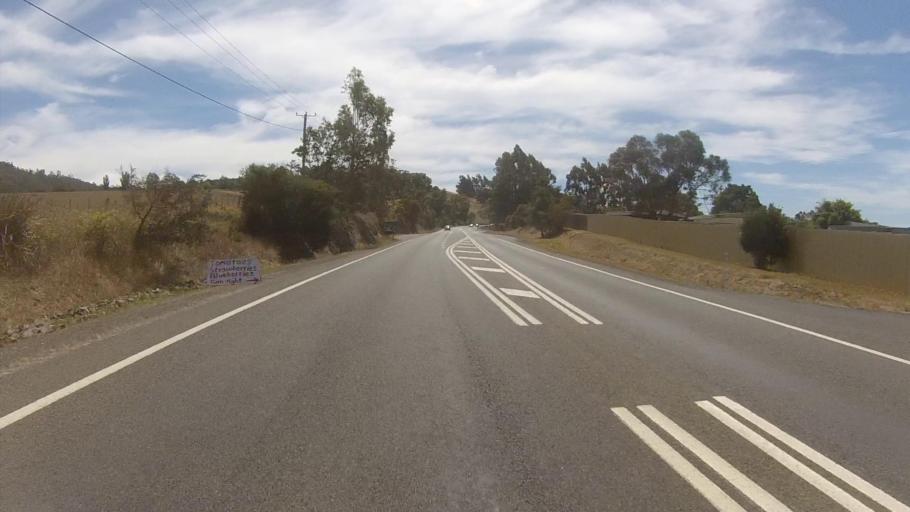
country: AU
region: Tasmania
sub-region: Kingborough
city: Margate
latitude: -43.0087
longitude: 147.2719
